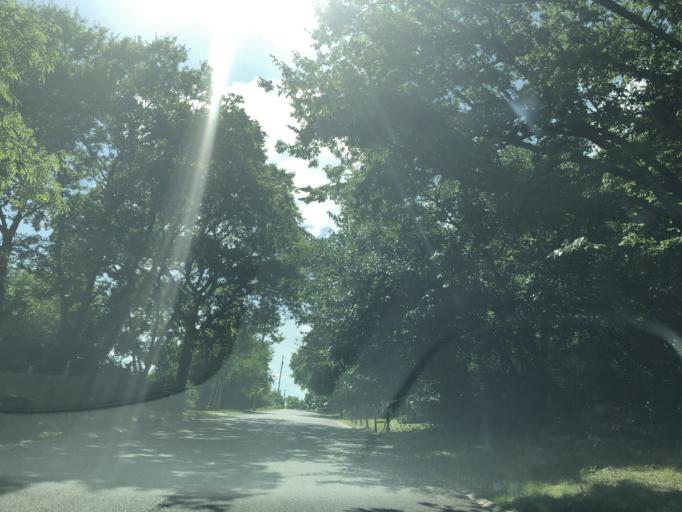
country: US
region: Tennessee
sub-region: Davidson County
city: Oak Hill
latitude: 36.1006
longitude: -86.7432
